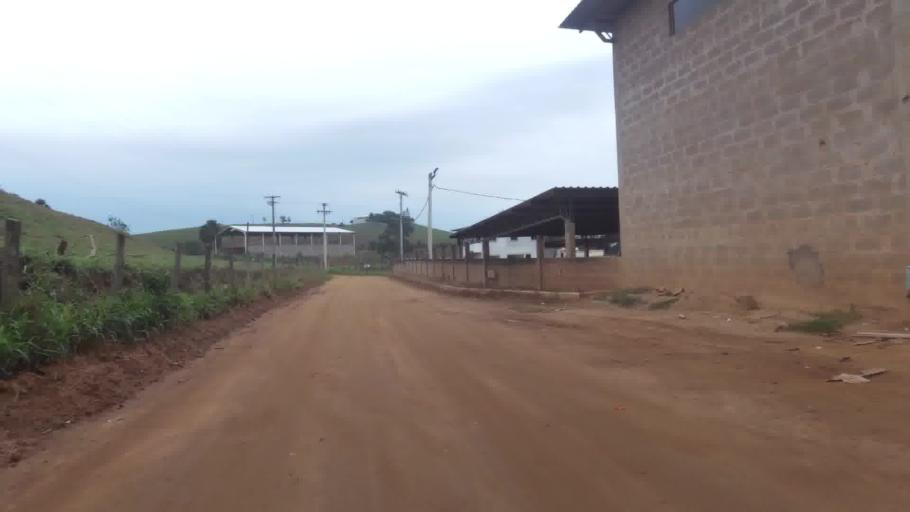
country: BR
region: Espirito Santo
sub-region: Iconha
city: Iconha
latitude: -20.8022
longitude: -40.8162
